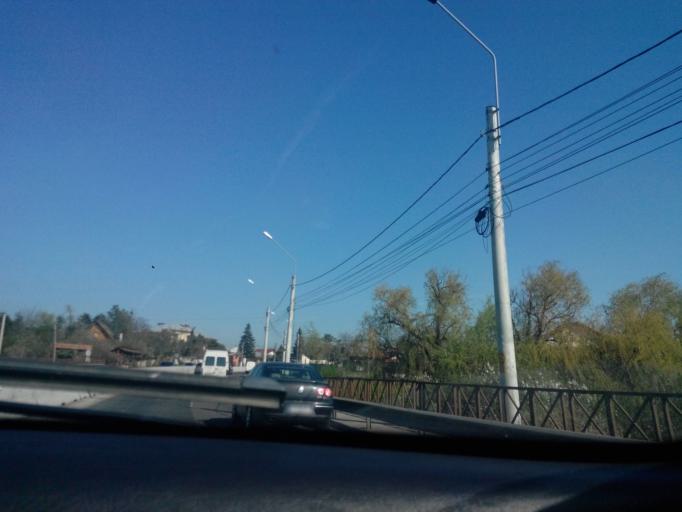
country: RO
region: Ilfov
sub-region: Comuna Corbeanca
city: Corbeanca
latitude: 44.6145
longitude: 26.0703
